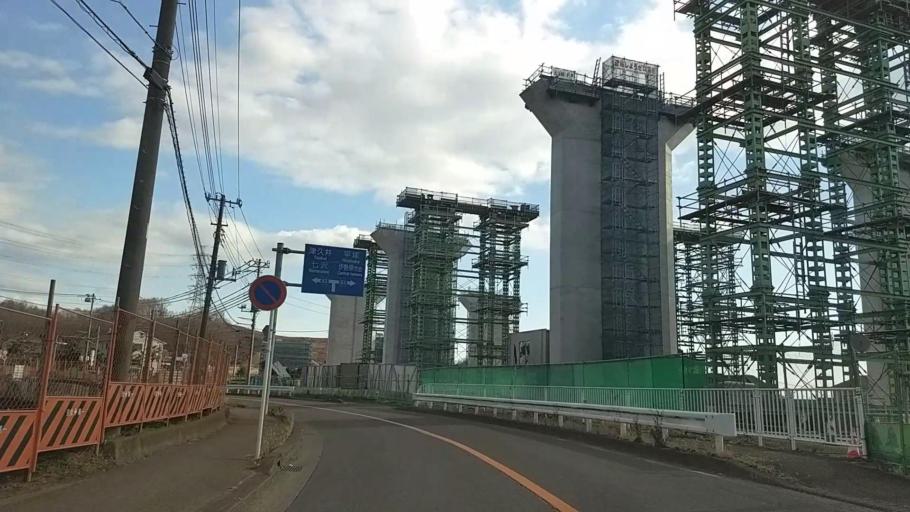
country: JP
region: Kanagawa
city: Isehara
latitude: 35.4157
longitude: 139.3015
